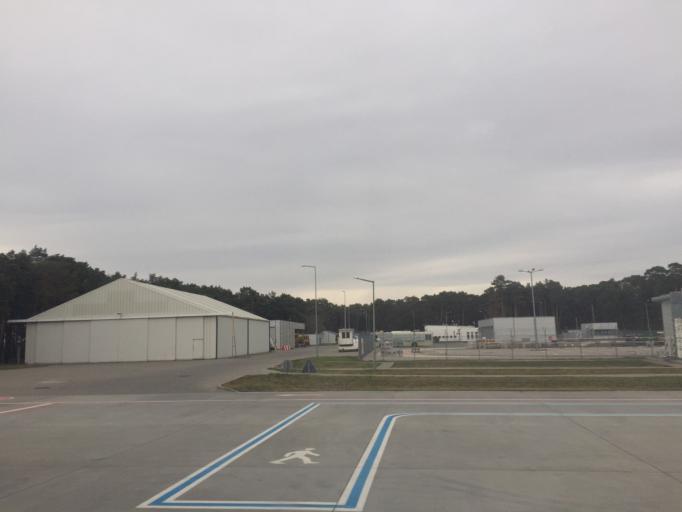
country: PL
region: Kujawsko-Pomorskie
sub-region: Bydgoszcz
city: Bydgoszcz
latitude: 53.0948
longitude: 17.9975
